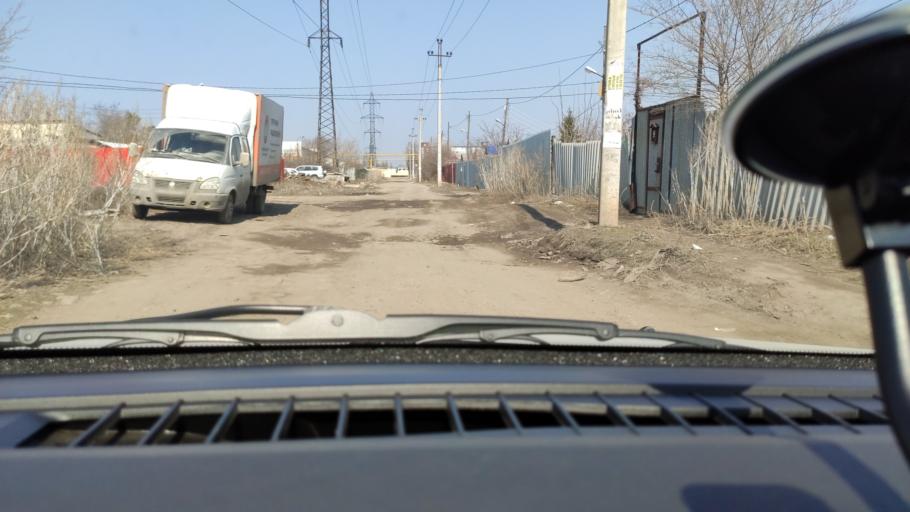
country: RU
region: Samara
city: Samara
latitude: 53.1819
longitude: 50.2371
